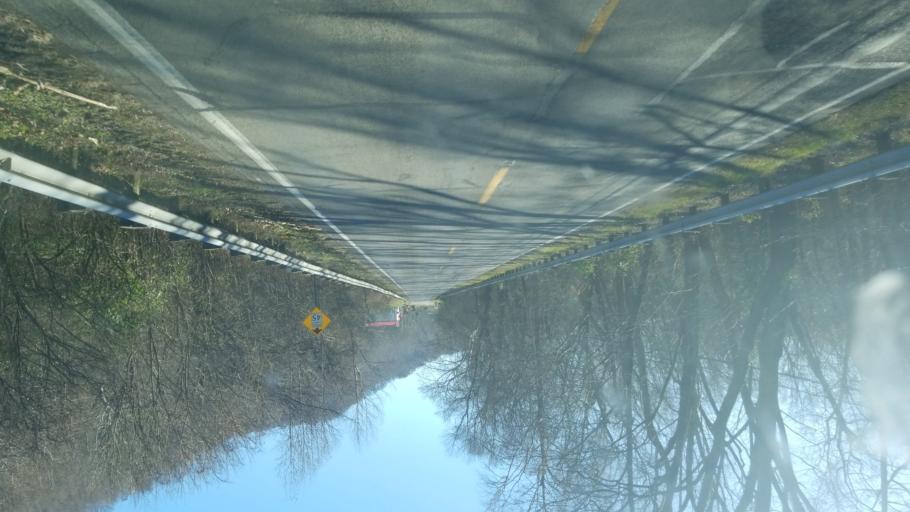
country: US
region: Kentucky
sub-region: Lewis County
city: Vanceburg
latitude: 38.6302
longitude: -83.2566
